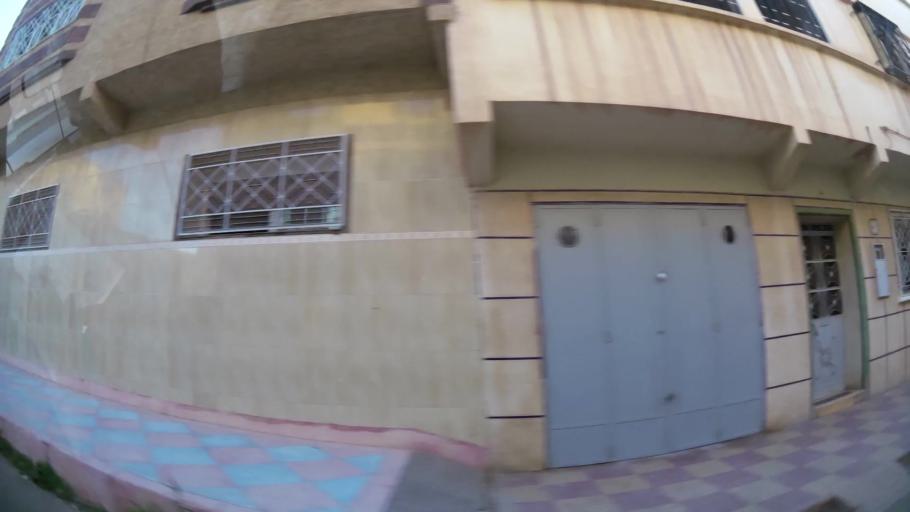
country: MA
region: Oriental
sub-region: Oujda-Angad
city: Oujda
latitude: 34.7064
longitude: -1.9143
